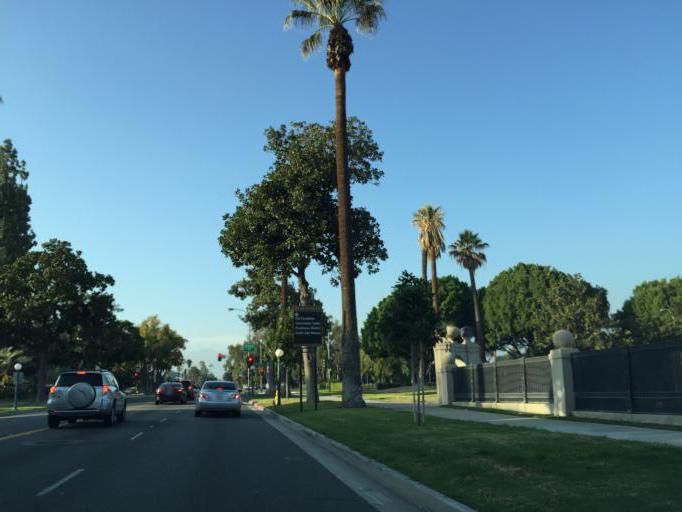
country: US
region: California
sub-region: Los Angeles County
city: Pasadena
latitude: 34.1439
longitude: -118.1599
